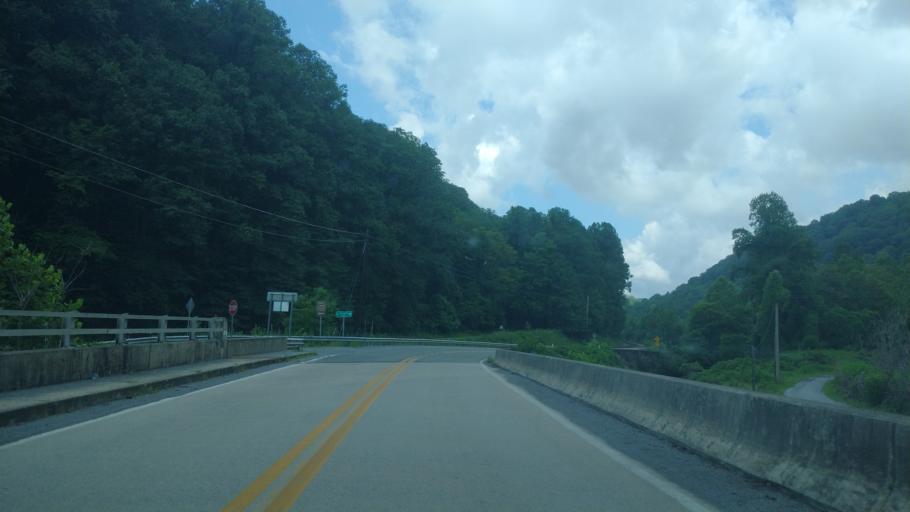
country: US
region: West Virginia
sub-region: McDowell County
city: Welch
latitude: 37.4107
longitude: -81.4712
